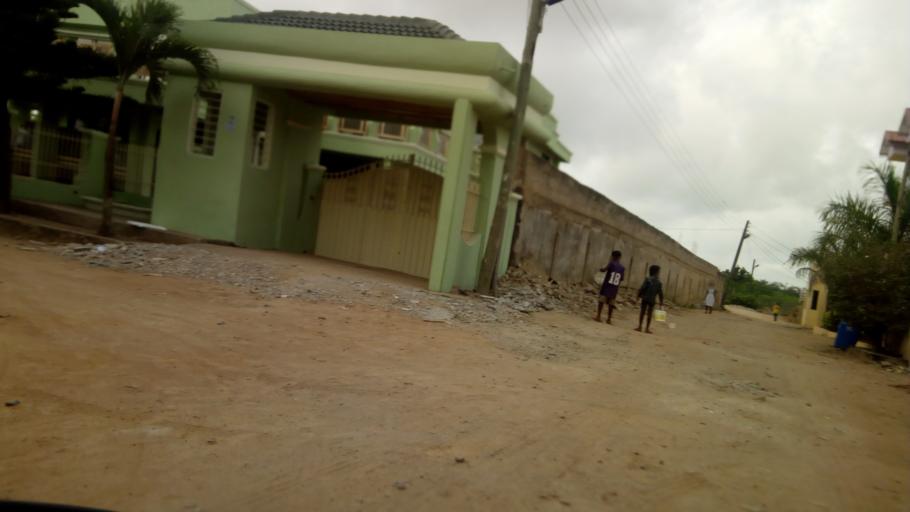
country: GH
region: Central
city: Cape Coast
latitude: 5.1256
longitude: -1.2780
